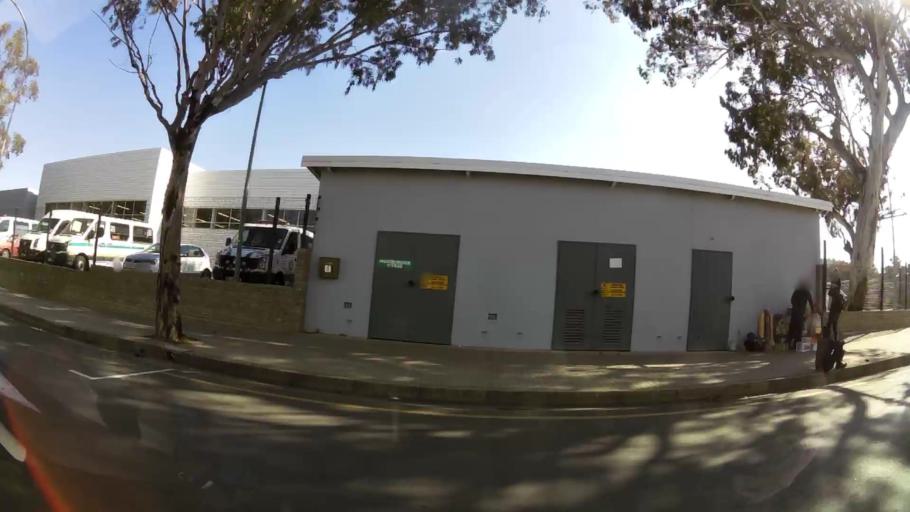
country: ZA
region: Orange Free State
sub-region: Mangaung Metropolitan Municipality
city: Bloemfontein
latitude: -29.1118
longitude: 26.2219
